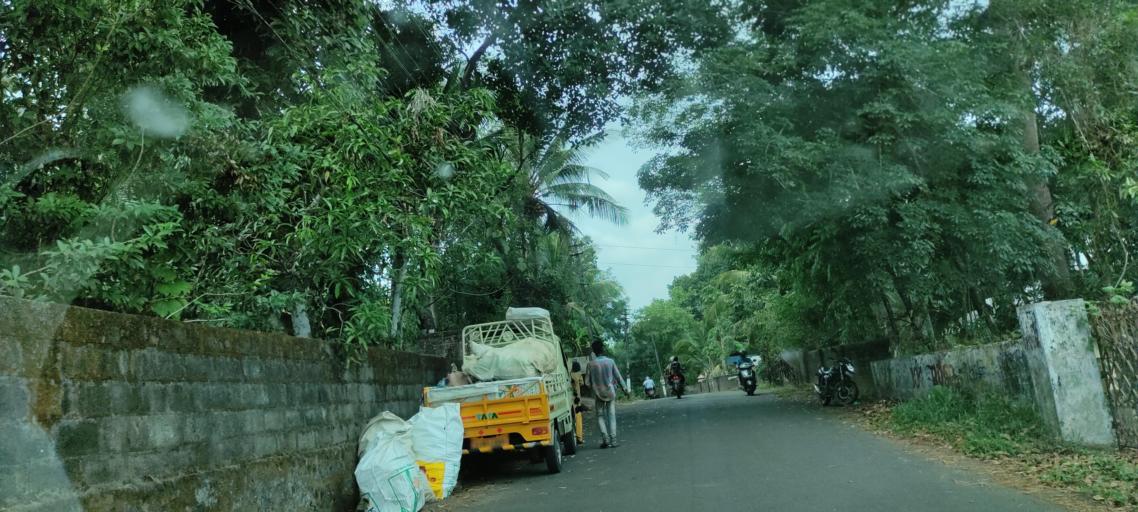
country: IN
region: Kerala
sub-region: Pattanamtitta
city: Adur
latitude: 9.1649
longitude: 76.7352
